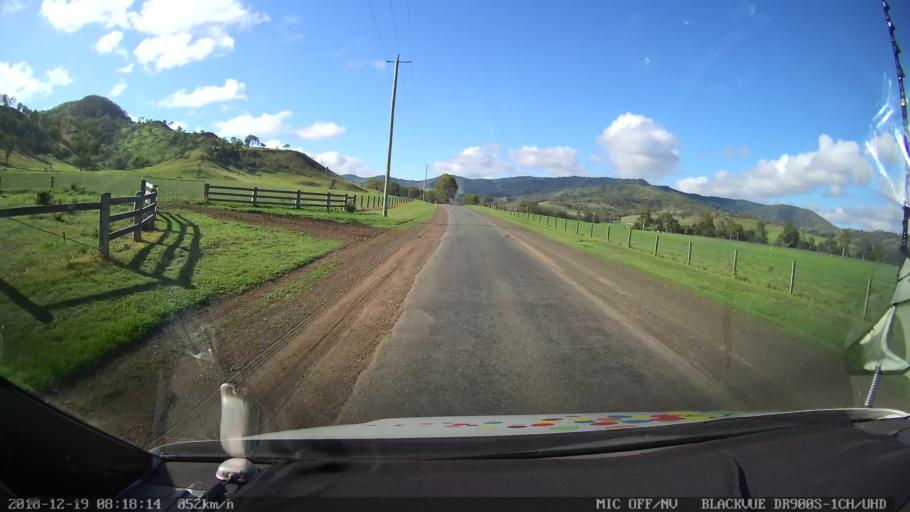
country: AU
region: New South Wales
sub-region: Kyogle
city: Kyogle
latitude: -28.2714
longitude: 152.9097
